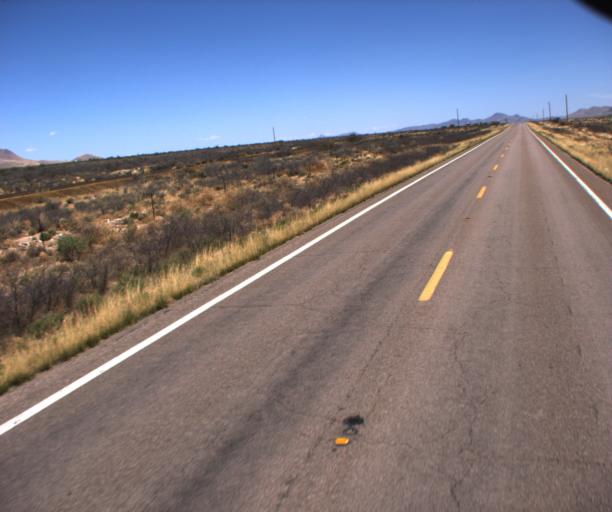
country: US
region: Arizona
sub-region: Cochise County
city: Douglas
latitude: 31.7534
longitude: -109.0891
